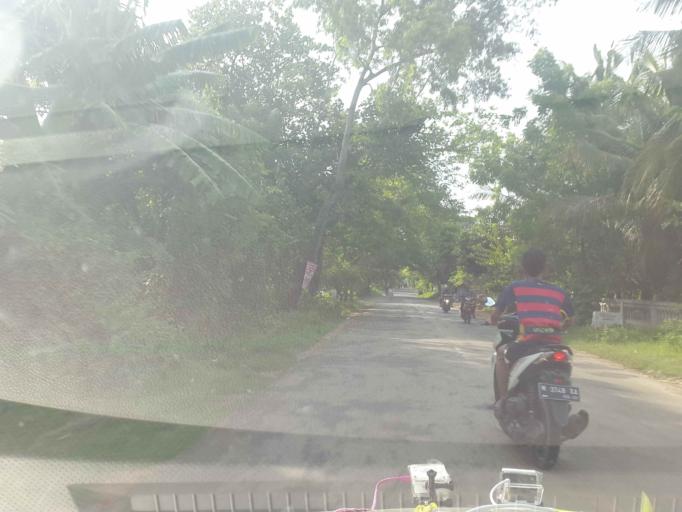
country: ID
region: East Java
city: Kebunkelapa
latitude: -7.0413
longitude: 113.9189
